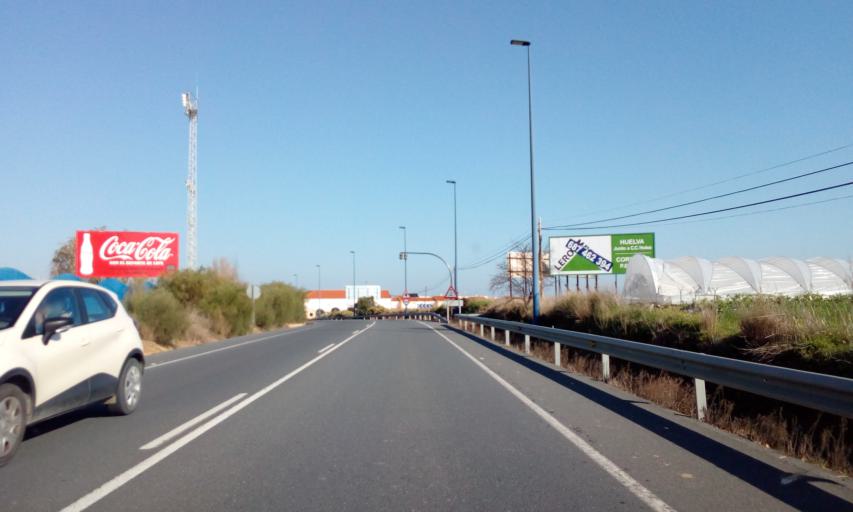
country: ES
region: Andalusia
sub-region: Provincia de Huelva
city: Lepe
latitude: 37.2440
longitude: -7.2042
